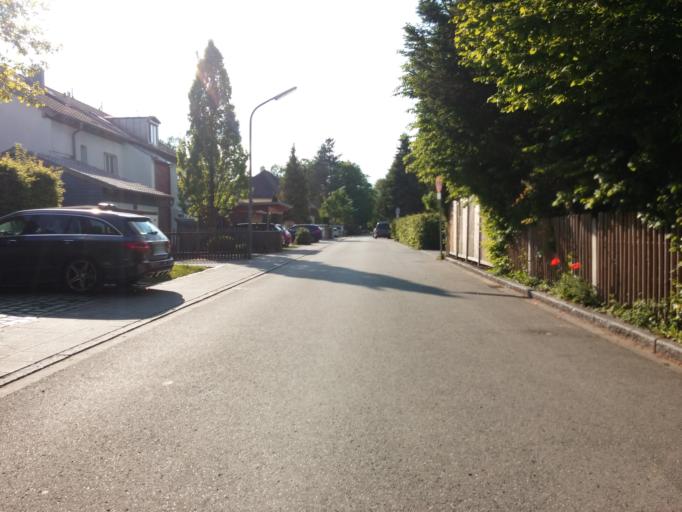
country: DE
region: Bavaria
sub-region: Upper Bavaria
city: Vaterstetten
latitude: 48.0929
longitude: 11.7837
